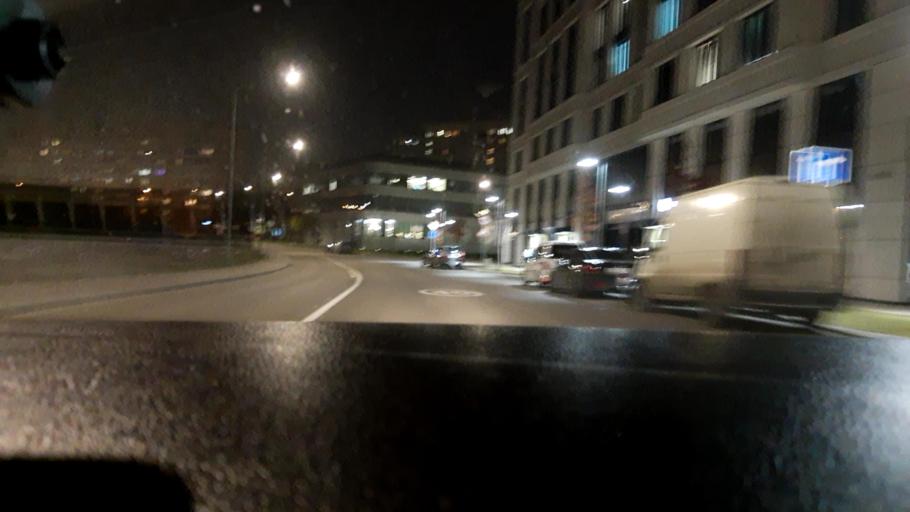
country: RU
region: Moskovskaya
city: Dorogomilovo
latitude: 55.7898
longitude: 37.5672
